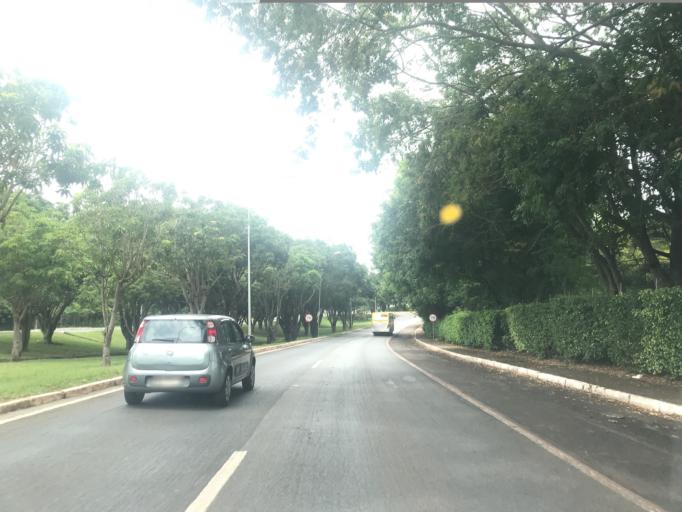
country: BR
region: Federal District
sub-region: Brasilia
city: Brasilia
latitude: -15.8400
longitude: -47.8387
